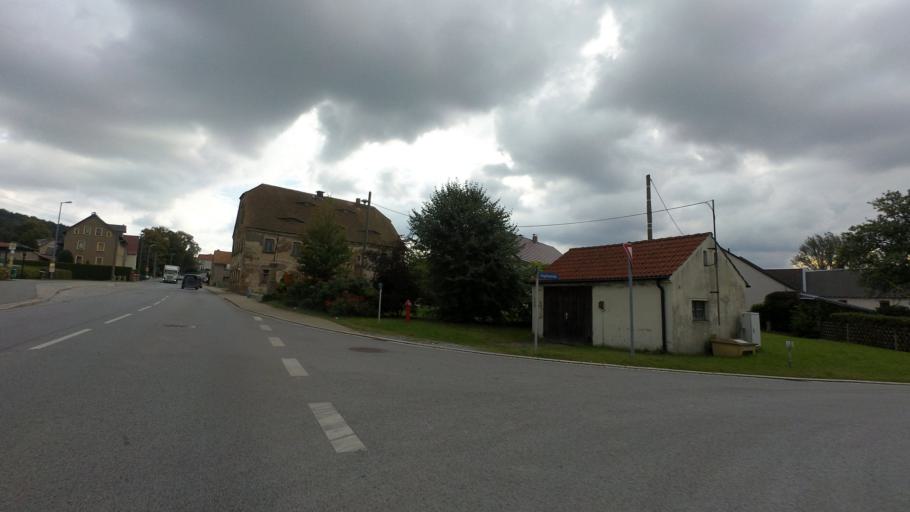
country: DE
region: Saxony
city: Grosspostwitz
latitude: 51.1401
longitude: 14.4414
